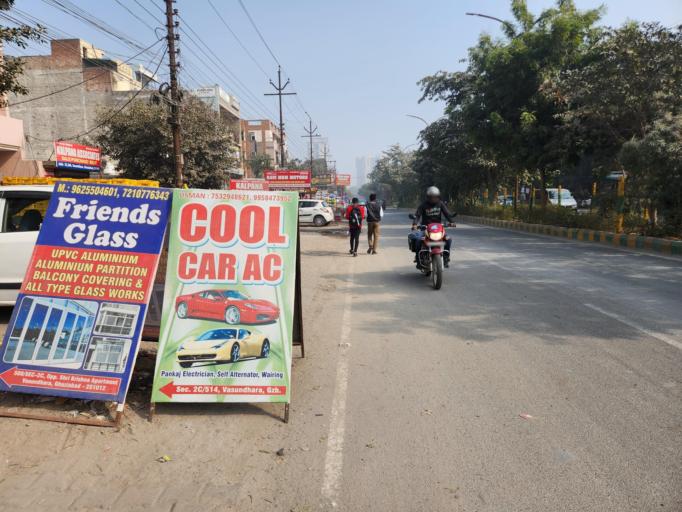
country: IN
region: Uttar Pradesh
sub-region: Ghaziabad
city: Ghaziabad
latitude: 28.6674
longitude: 77.3729
